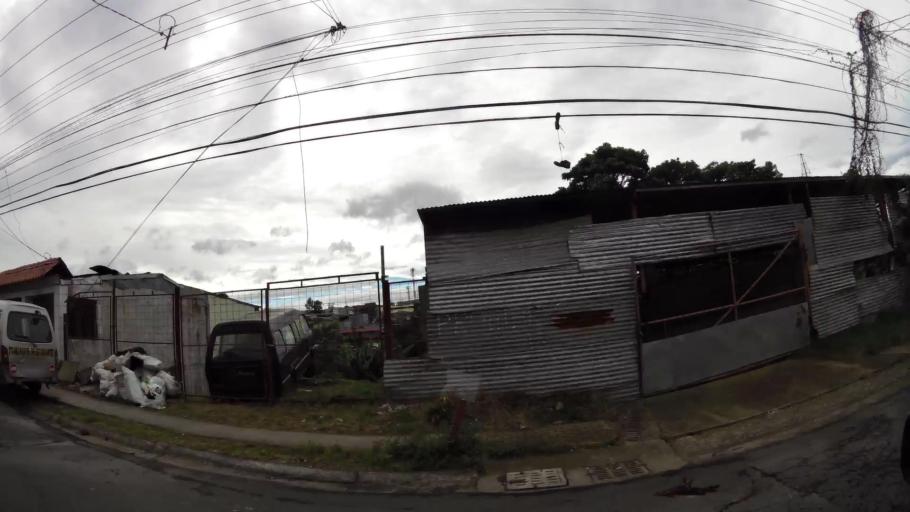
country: CR
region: San Jose
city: Purral
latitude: 9.9617
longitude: -84.0261
